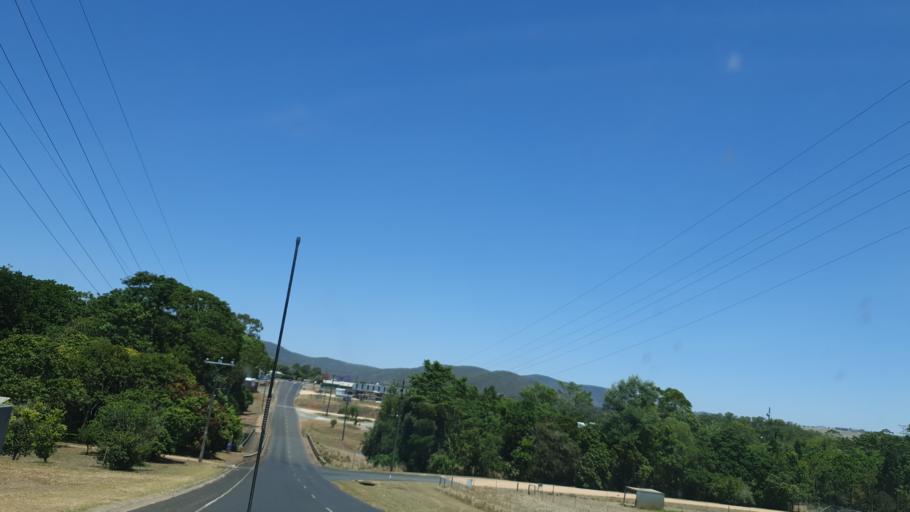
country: AU
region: Queensland
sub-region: Tablelands
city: Atherton
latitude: -17.2573
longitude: 145.4810
